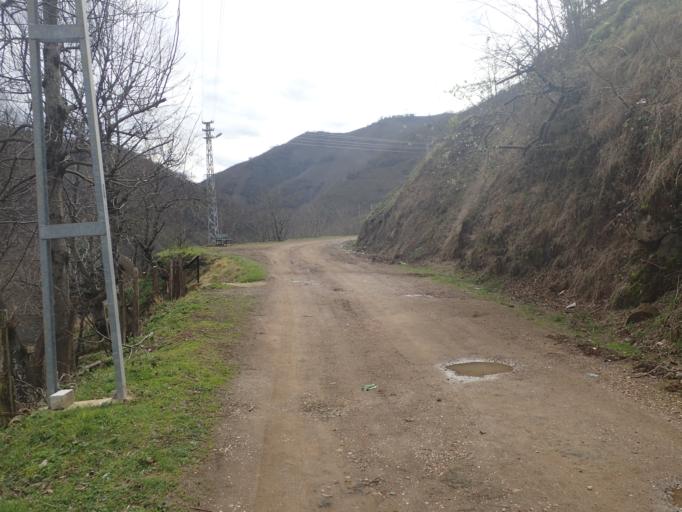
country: TR
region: Ordu
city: Camas
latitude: 40.9020
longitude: 37.5751
